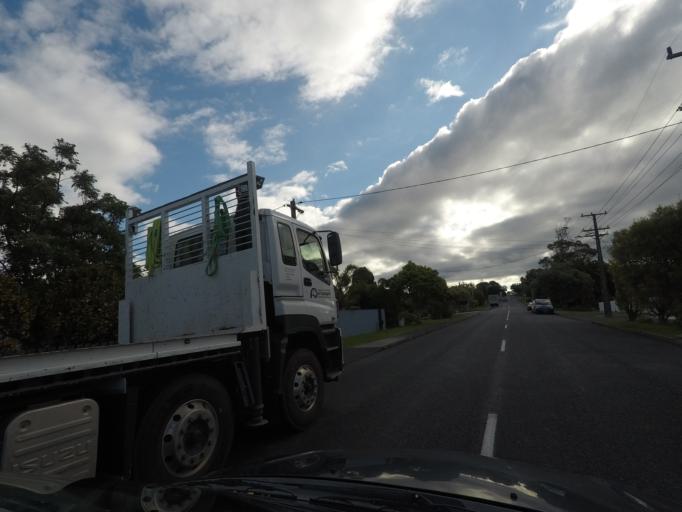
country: NZ
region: Auckland
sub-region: Auckland
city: Rosebank
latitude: -36.8851
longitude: 174.6496
